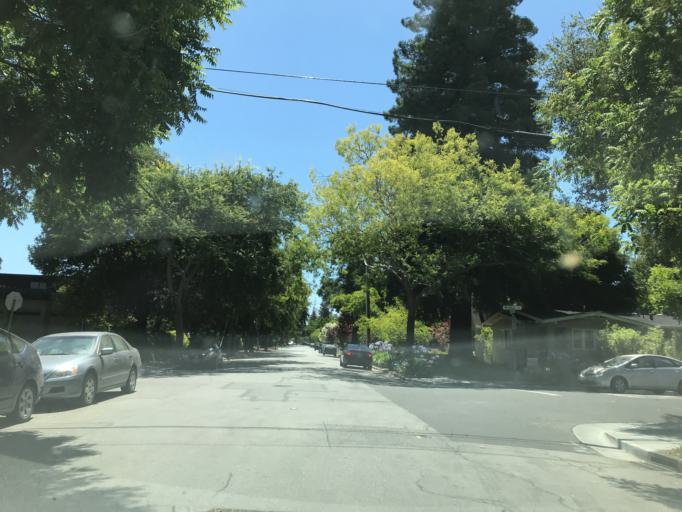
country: US
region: California
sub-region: Santa Clara County
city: Palo Alto
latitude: 37.4386
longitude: -122.1532
